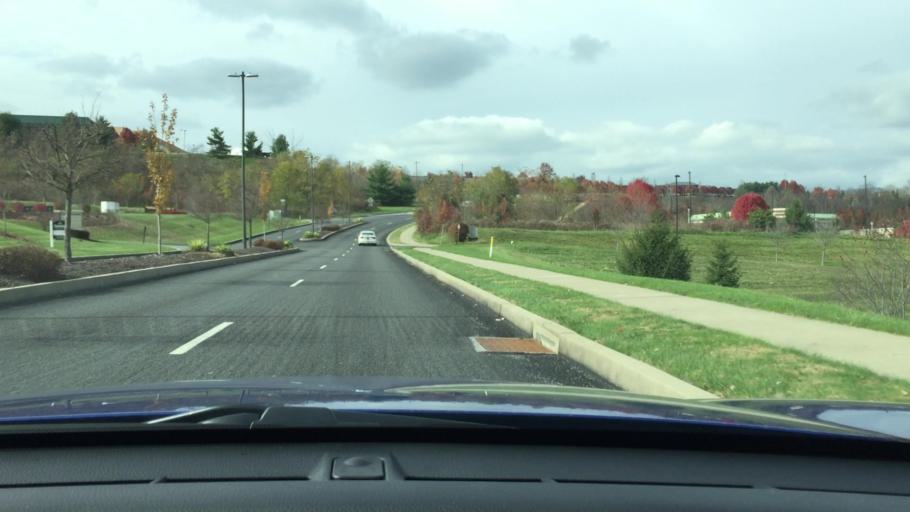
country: US
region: Pennsylvania
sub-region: Washington County
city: Canonsburg
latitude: 40.2786
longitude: -80.1683
